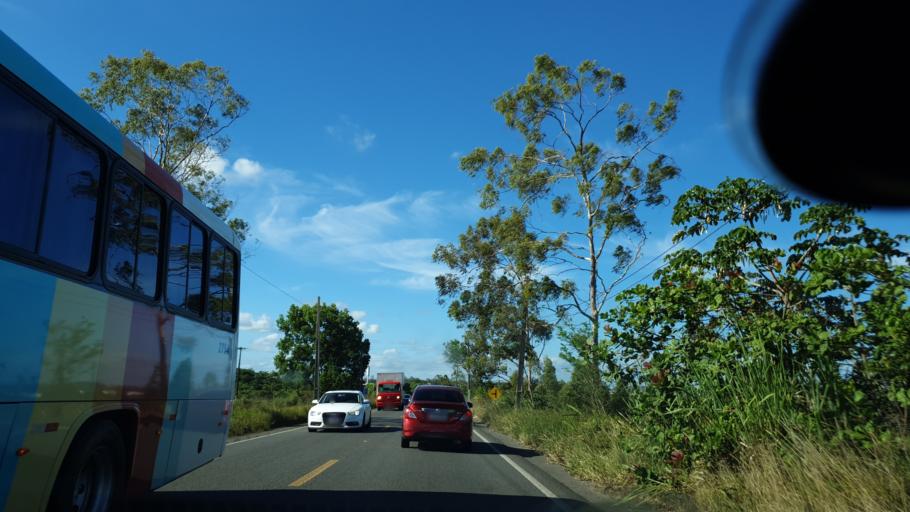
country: BR
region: Bahia
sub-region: Camacari
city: Camacari
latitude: -12.6522
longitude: -38.3032
